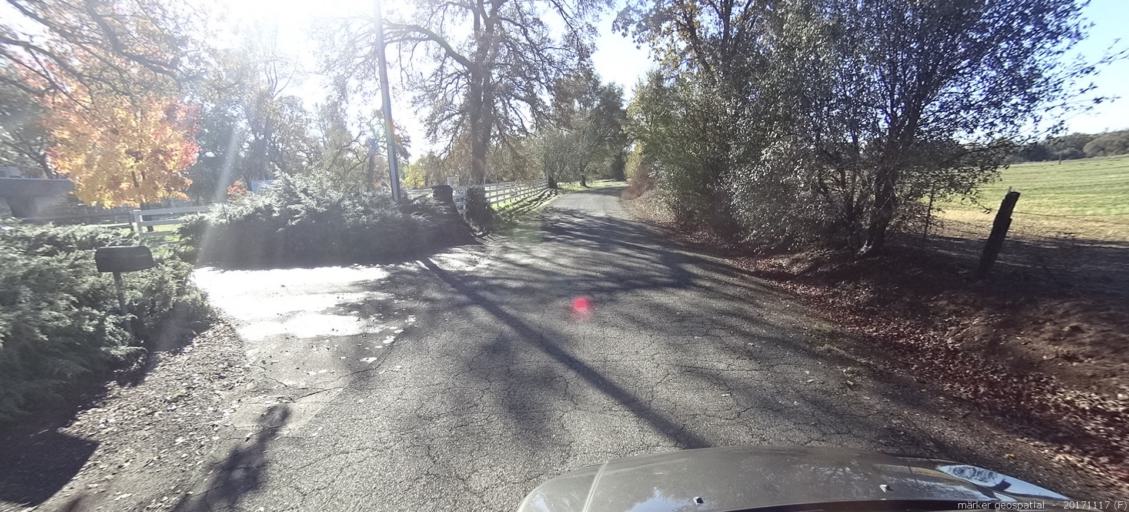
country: US
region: California
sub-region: Shasta County
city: Anderson
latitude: 40.4522
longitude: -122.1959
